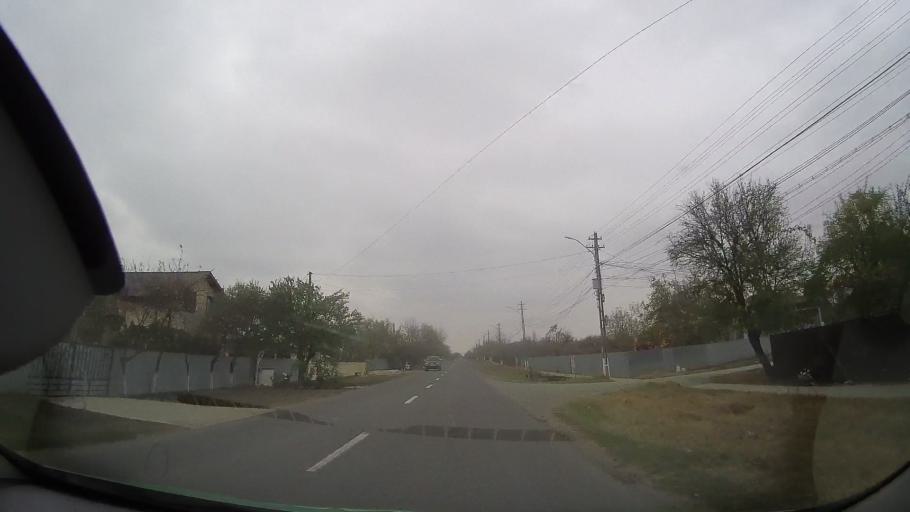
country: RO
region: Ialomita
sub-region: Comuna Garbovi
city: Garbovi
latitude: 44.7829
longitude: 26.7681
